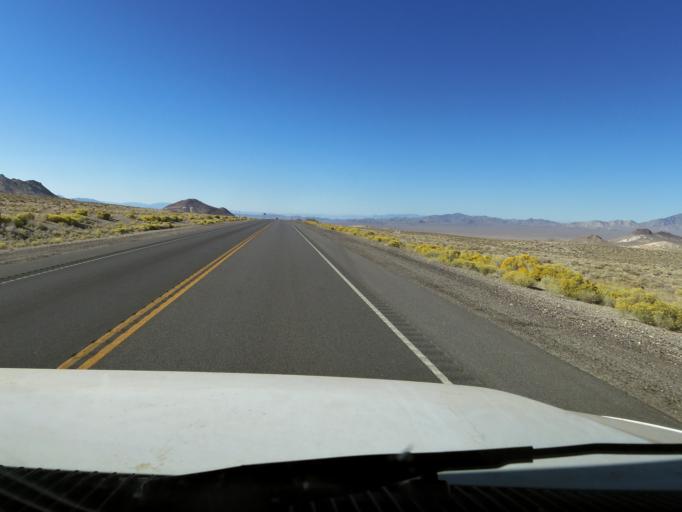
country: US
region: Nevada
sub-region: Nye County
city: Tonopah
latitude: 38.0272
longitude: -117.2375
